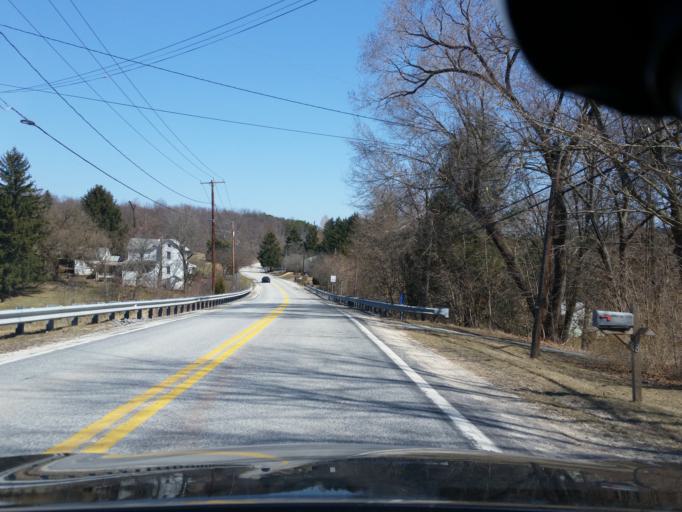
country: US
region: Pennsylvania
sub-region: Perry County
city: Marysville
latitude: 40.3265
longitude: -76.9920
